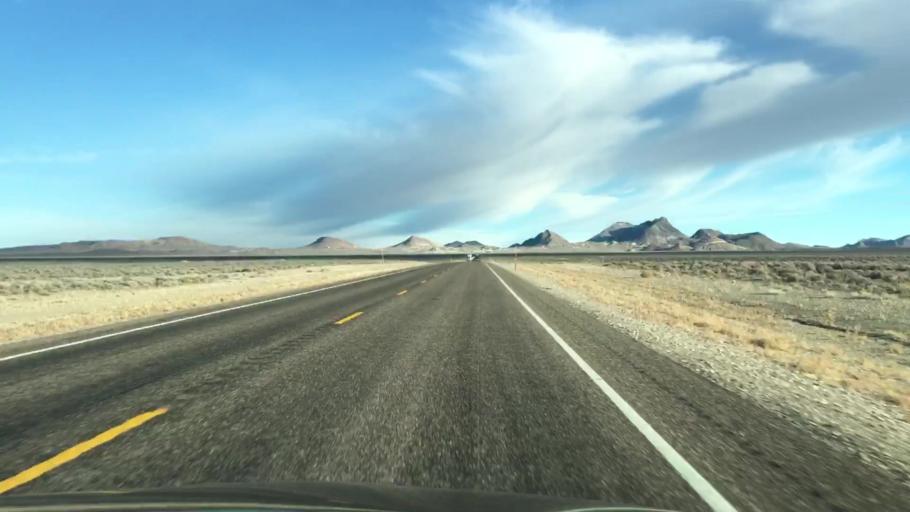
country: US
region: Nevada
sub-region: Nye County
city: Tonopah
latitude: 38.0996
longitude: -117.3272
